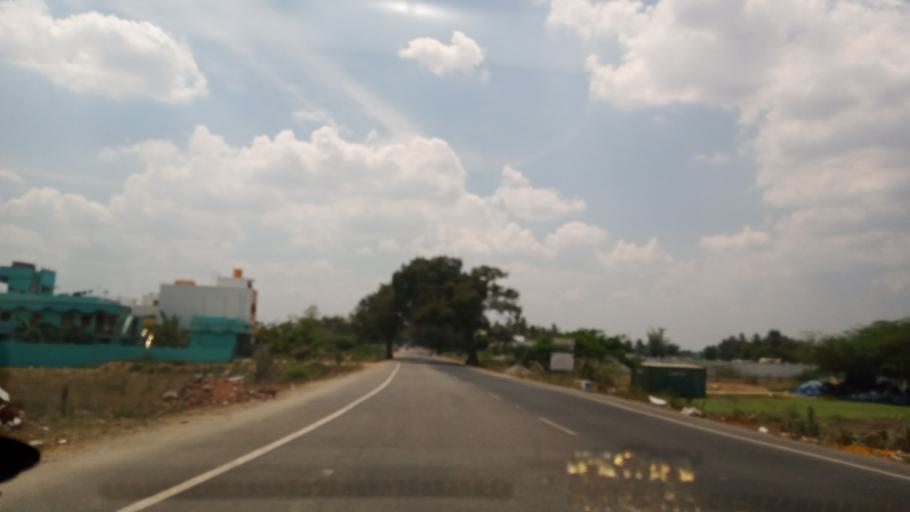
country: IN
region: Tamil Nadu
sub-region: Vellore
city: Walajapet
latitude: 12.9183
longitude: 79.3857
